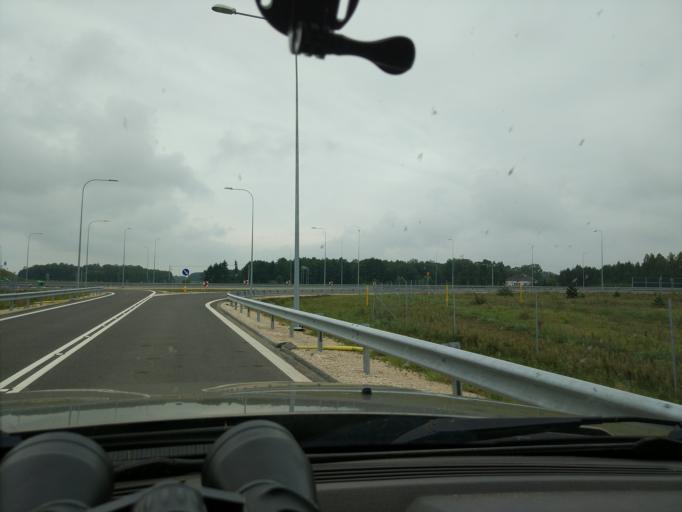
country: PL
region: Podlasie
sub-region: Powiat zambrowski
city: Szumowo
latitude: 52.9107
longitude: 22.0960
